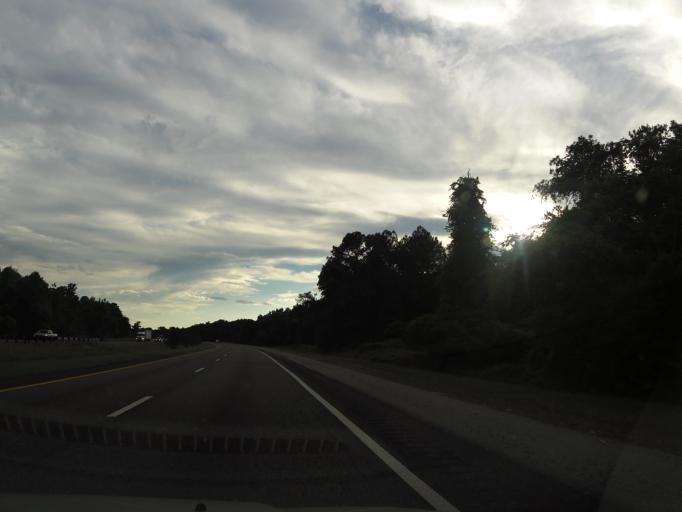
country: US
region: South Carolina
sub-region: Jasper County
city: Hardeeville
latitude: 32.2535
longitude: -81.1251
